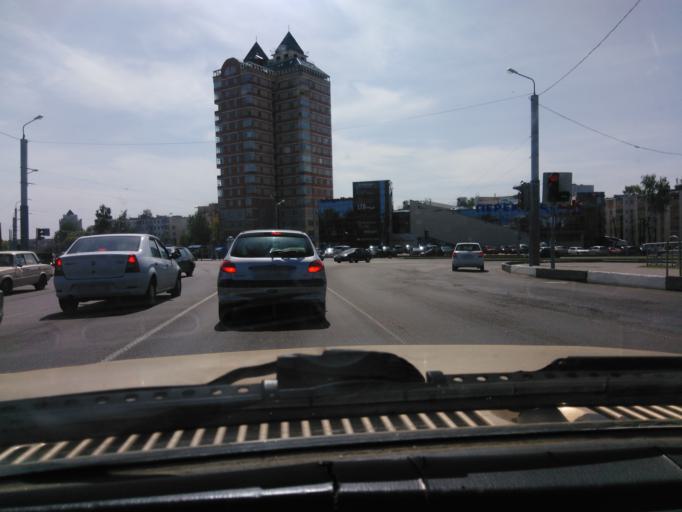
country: BY
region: Mogilev
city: Mahilyow
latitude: 53.9133
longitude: 30.3181
